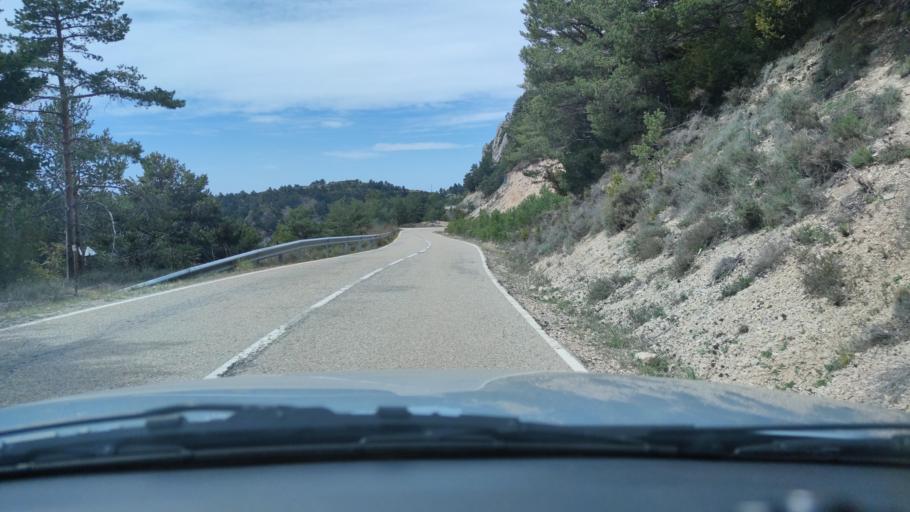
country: ES
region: Catalonia
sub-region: Provincia de Lleida
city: Olius
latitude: 42.1430
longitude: 1.5506
